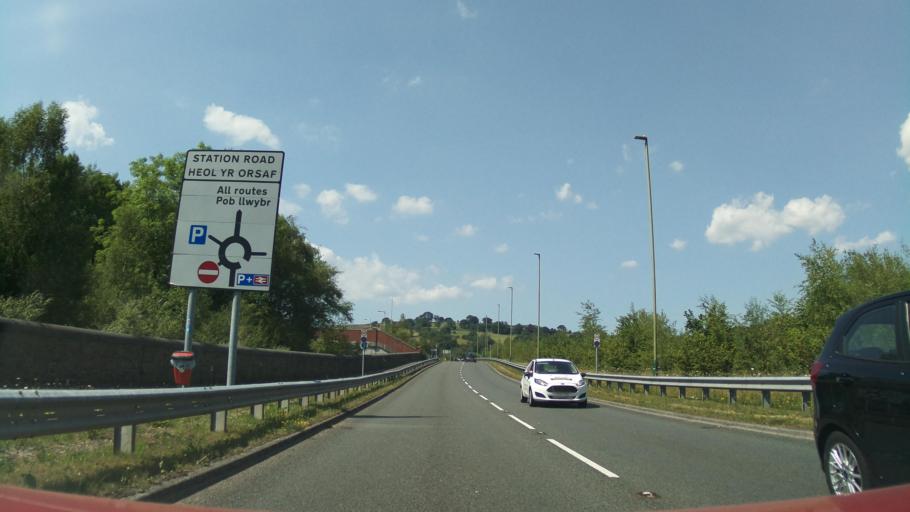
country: GB
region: Wales
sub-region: Caerphilly County Borough
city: Bargoed
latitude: 51.6899
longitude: -3.2271
